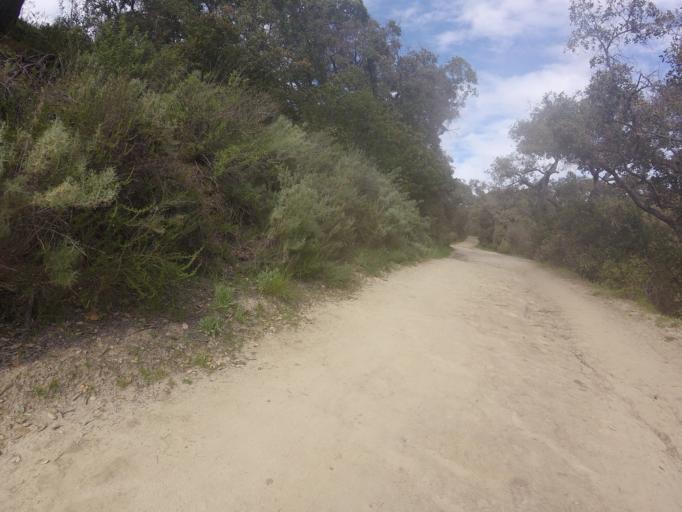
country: US
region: California
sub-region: Orange County
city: Aliso Viejo
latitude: 33.5762
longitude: -117.7479
